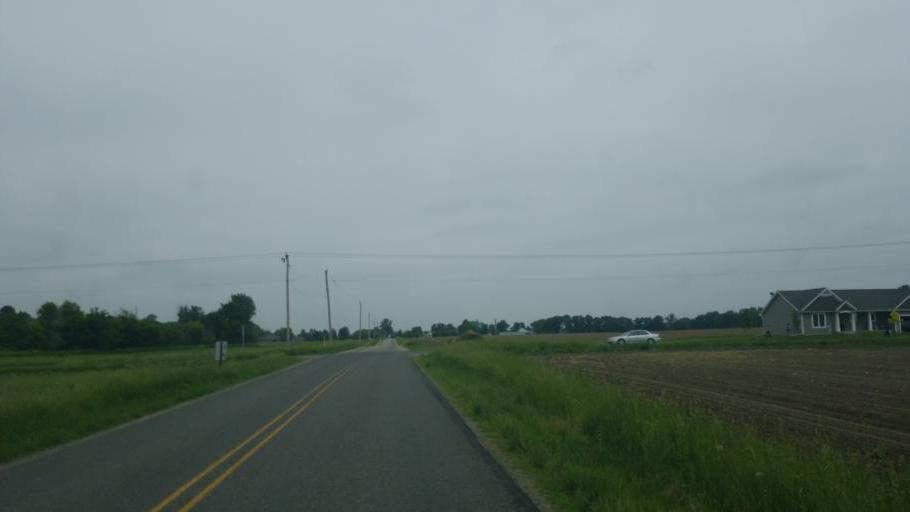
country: US
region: Indiana
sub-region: Elkhart County
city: Nappanee
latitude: 41.4567
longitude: -86.0207
